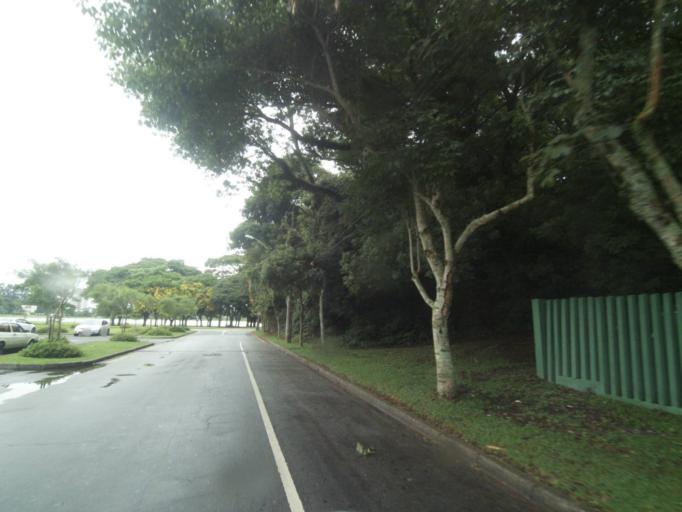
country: BR
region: Parana
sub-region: Curitiba
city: Curitiba
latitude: -25.4266
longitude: -49.3089
